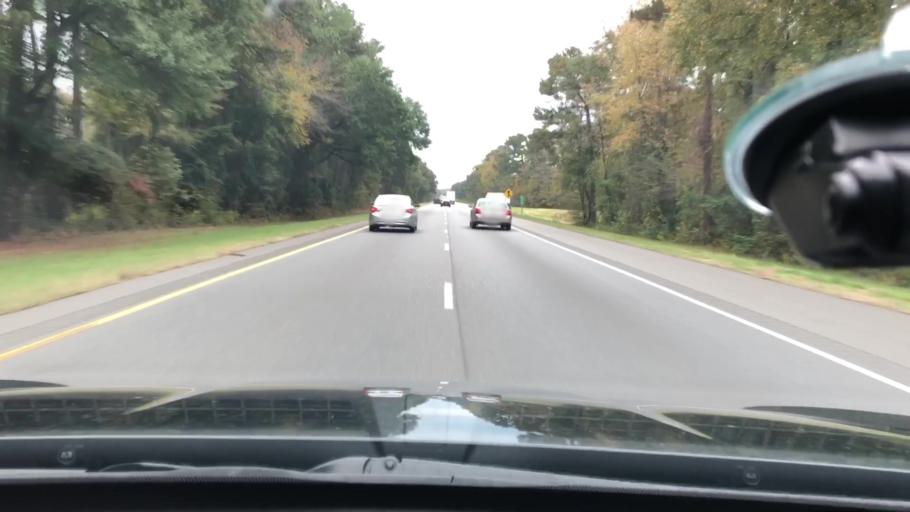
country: US
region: Arkansas
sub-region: Hempstead County
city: Hope
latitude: 33.6504
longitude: -93.6704
